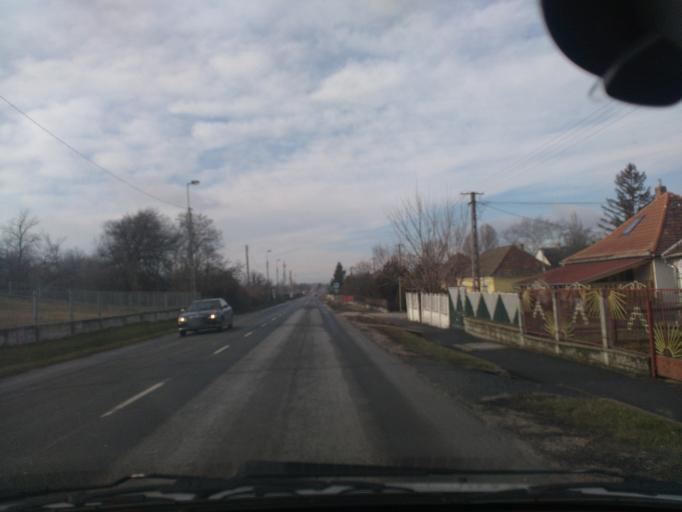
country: HU
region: Komarom-Esztergom
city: Tokod
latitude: 47.7333
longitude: 18.6852
